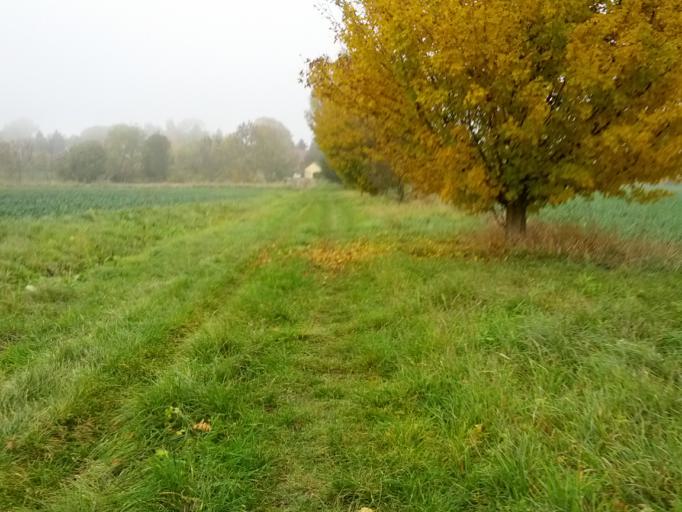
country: DE
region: Thuringia
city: Bischofroda
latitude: 51.0081
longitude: 10.3672
